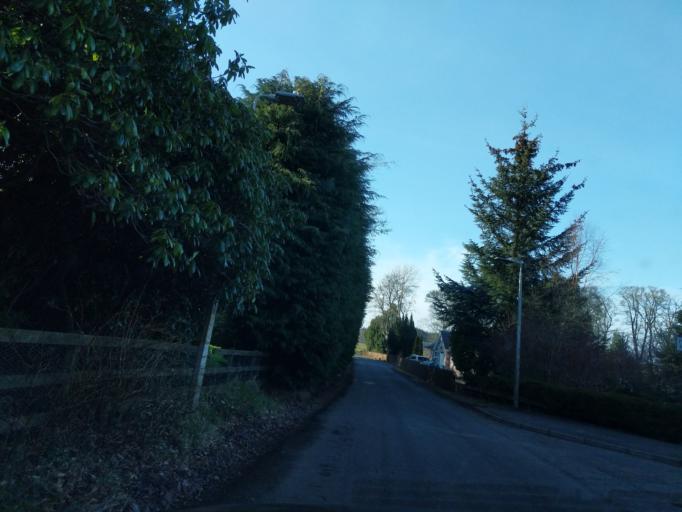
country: GB
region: Scotland
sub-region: The Scottish Borders
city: West Linton
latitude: 55.7088
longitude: -3.4368
